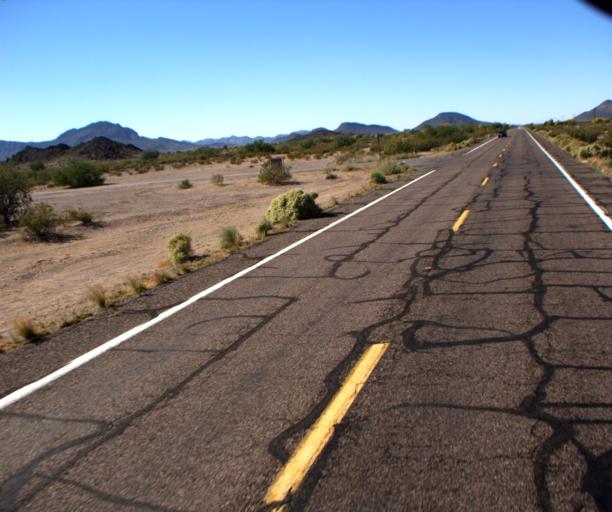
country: US
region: Arizona
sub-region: Maricopa County
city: Gila Bend
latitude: 32.8122
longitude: -112.7928
